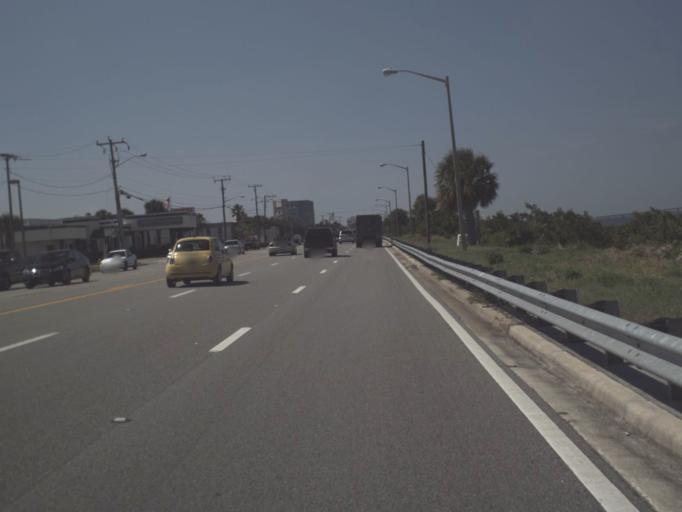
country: US
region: Florida
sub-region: Brevard County
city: Melbourne
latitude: 28.1020
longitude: -80.6140
